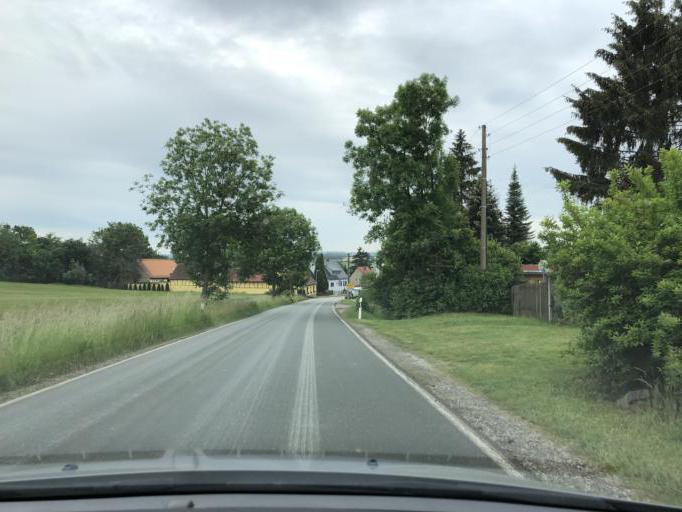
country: DE
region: Thuringia
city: Ossmanstedt
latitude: 51.0223
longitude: 11.4241
